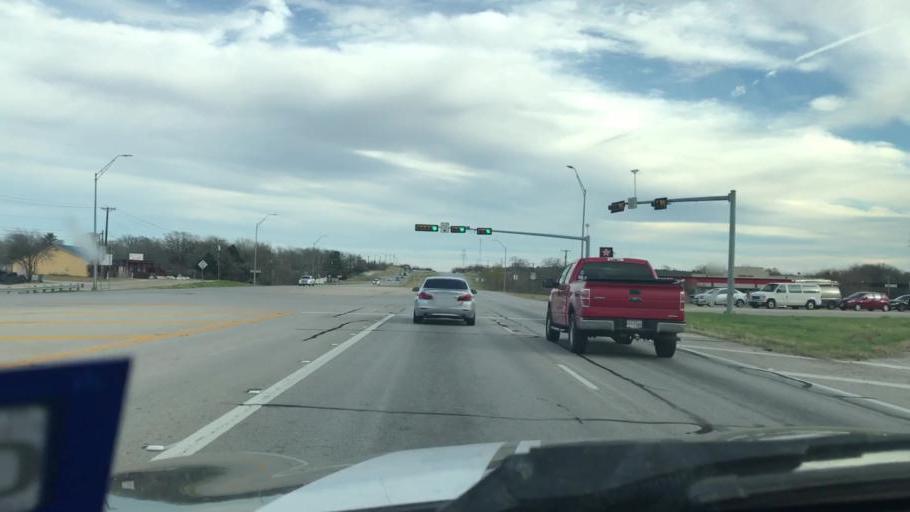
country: US
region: Texas
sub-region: Bastrop County
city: Elgin
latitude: 30.3350
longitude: -97.3621
